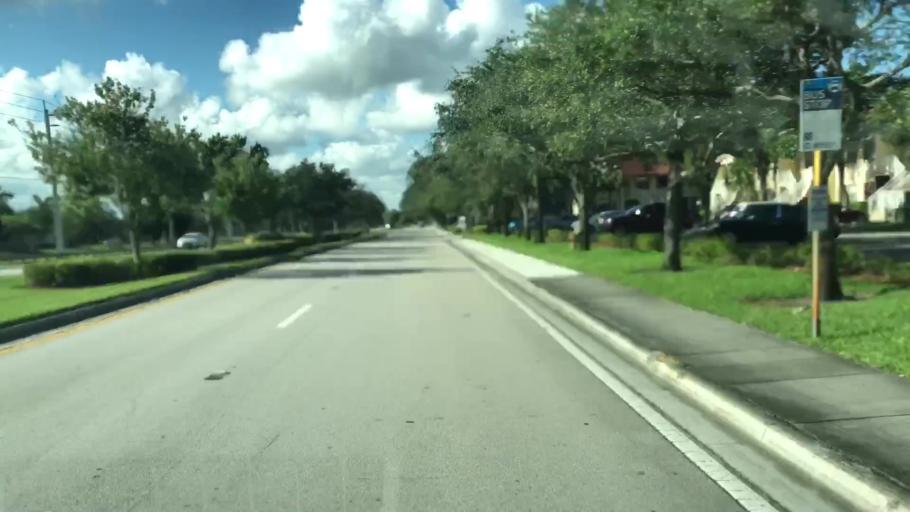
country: US
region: Florida
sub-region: Broward County
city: Coral Springs
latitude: 26.2654
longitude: -80.2663
